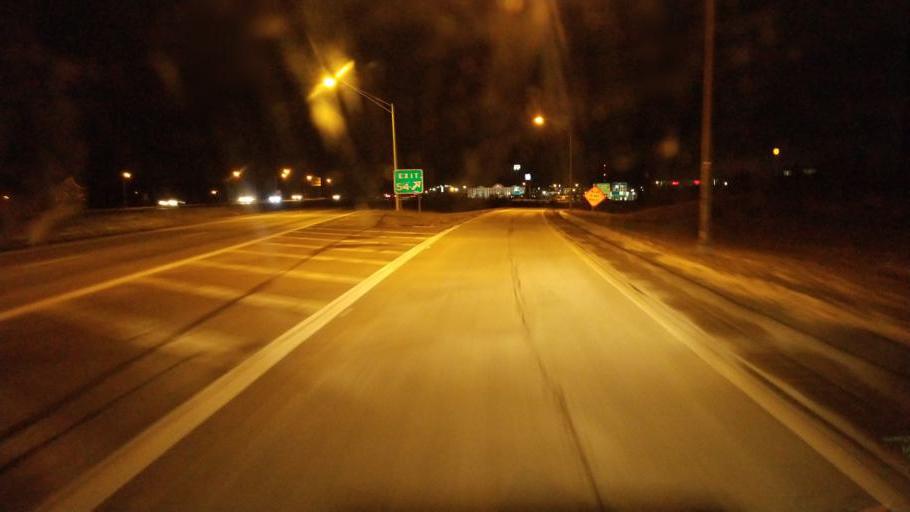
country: US
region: Ohio
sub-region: Clark County
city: Springfield
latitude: 39.8916
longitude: -83.8073
